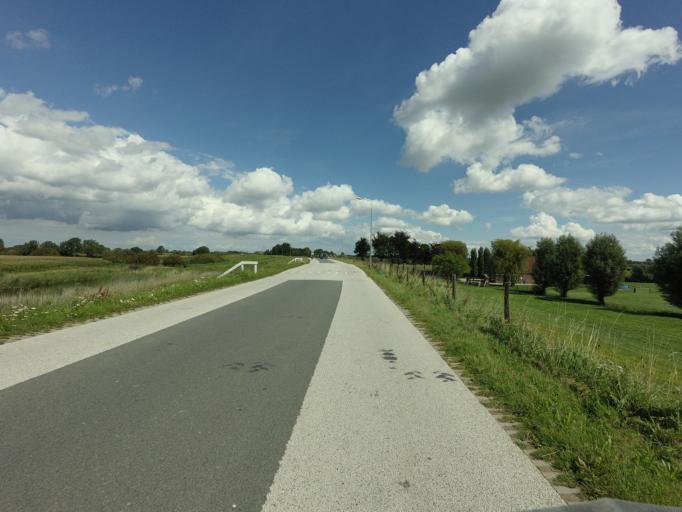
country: NL
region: Utrecht
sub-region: Gemeente Lopik
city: Lopik
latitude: 51.9709
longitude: 4.9944
